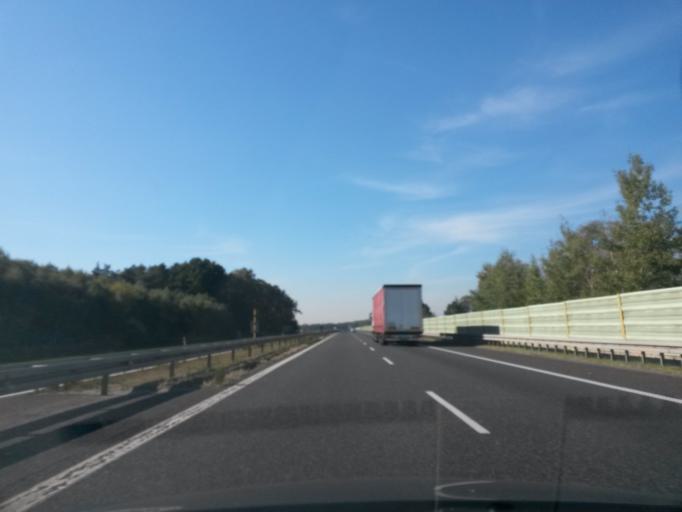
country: PL
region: Silesian Voivodeship
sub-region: Powiat gliwicki
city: Rudziniec
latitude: 50.3757
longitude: 18.4791
